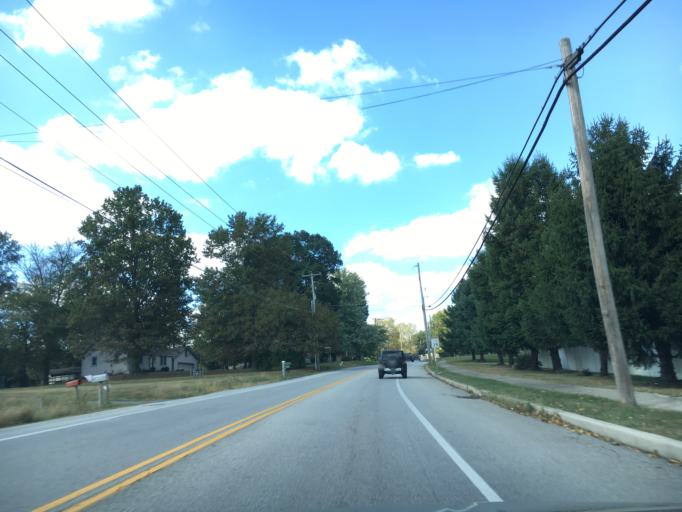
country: US
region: Pennsylvania
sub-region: York County
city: East York
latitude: 39.9959
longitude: -76.6755
